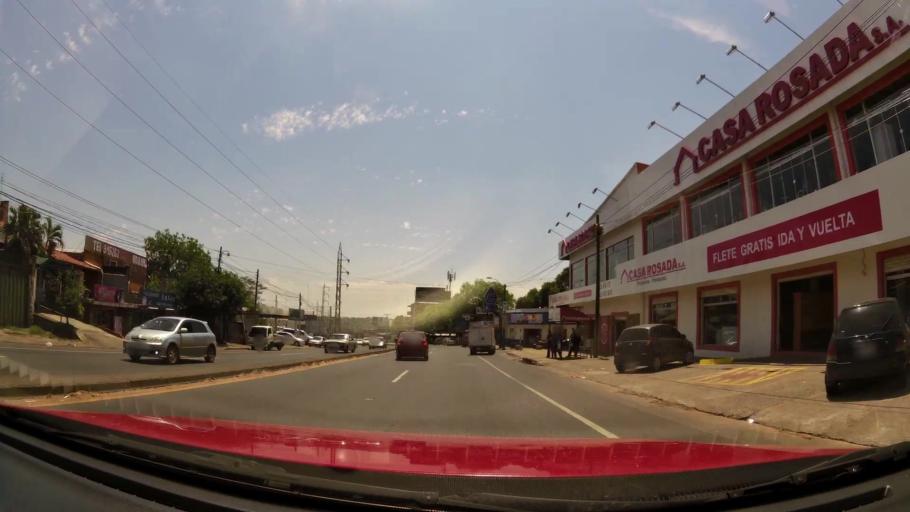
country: PY
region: Central
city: Lambare
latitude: -25.3418
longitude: -57.5823
